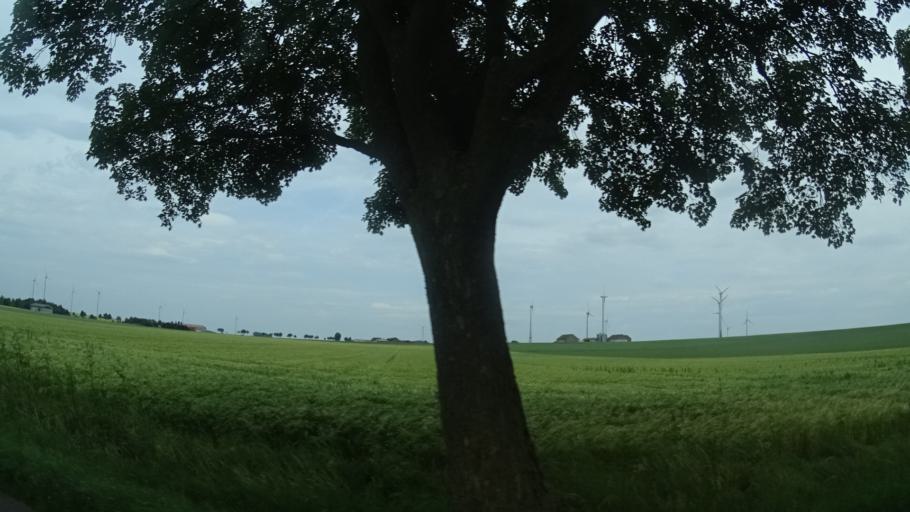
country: DE
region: North Rhine-Westphalia
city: Warburg
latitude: 51.5878
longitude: 9.1322
